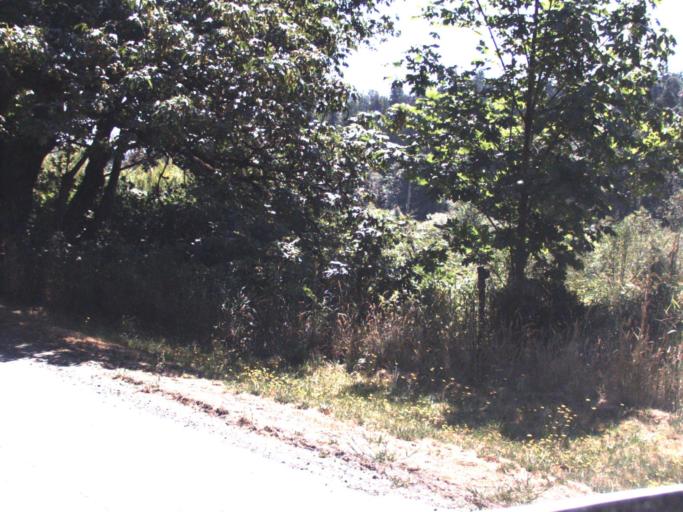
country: US
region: Washington
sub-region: King County
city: Ames Lake
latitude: 47.6275
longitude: -121.9843
